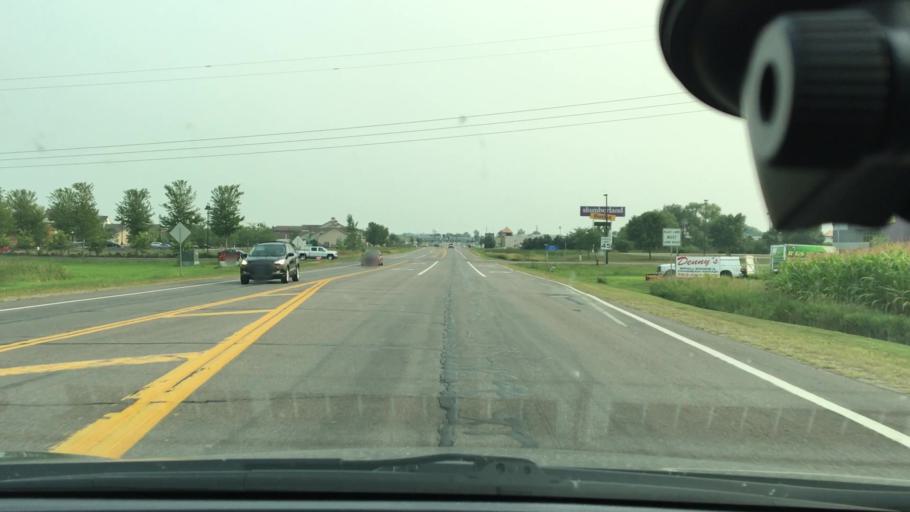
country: US
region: Minnesota
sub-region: Wright County
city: Albertville
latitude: 45.2492
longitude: -93.6634
